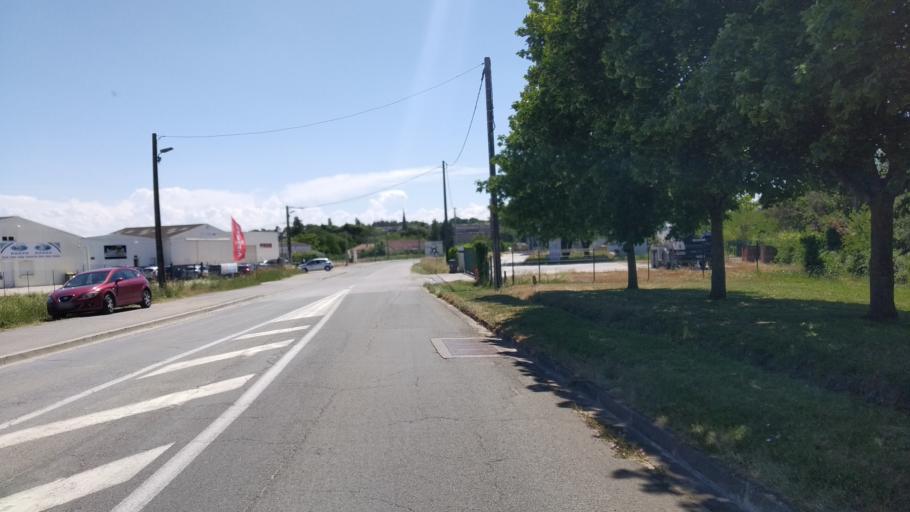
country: FR
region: Poitou-Charentes
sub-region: Departement de la Vienne
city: Biard
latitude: 46.6005
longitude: 0.3045
